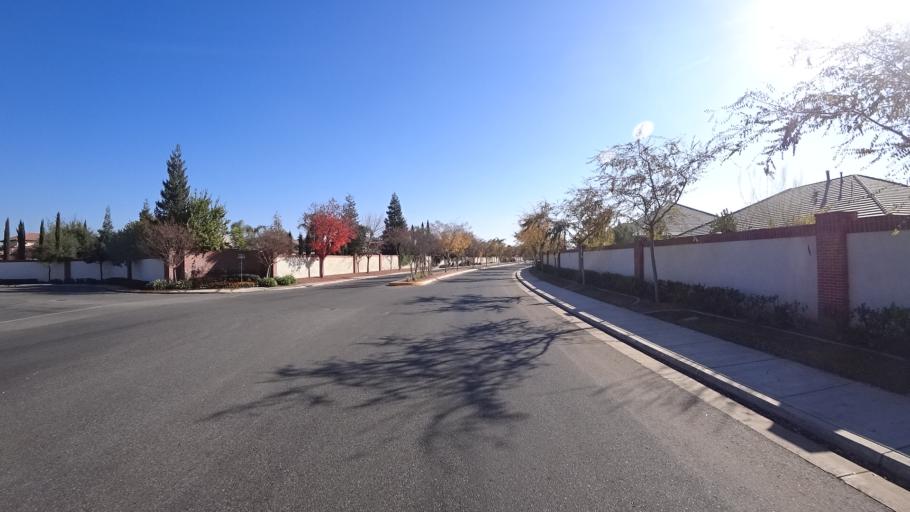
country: US
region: California
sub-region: Kern County
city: Rosedale
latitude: 35.3313
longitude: -119.1428
